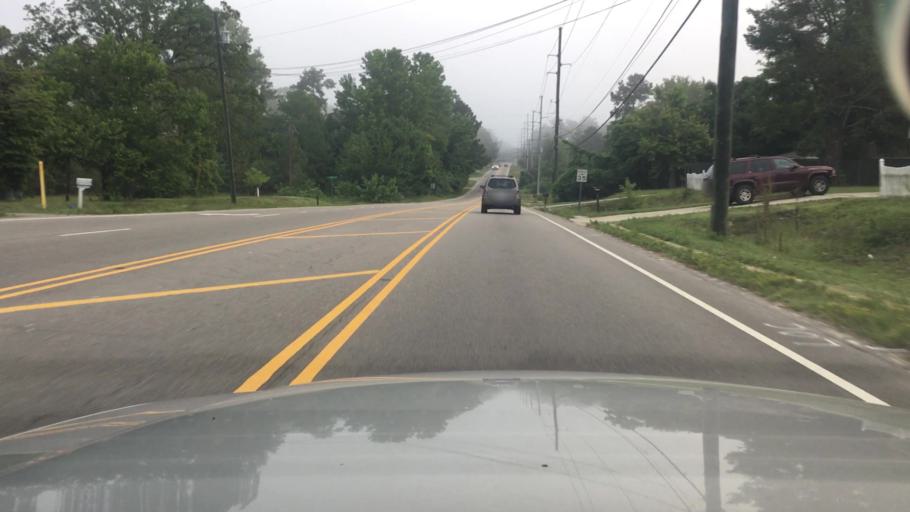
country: US
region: North Carolina
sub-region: Cumberland County
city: Hope Mills
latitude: 35.0151
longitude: -78.9400
